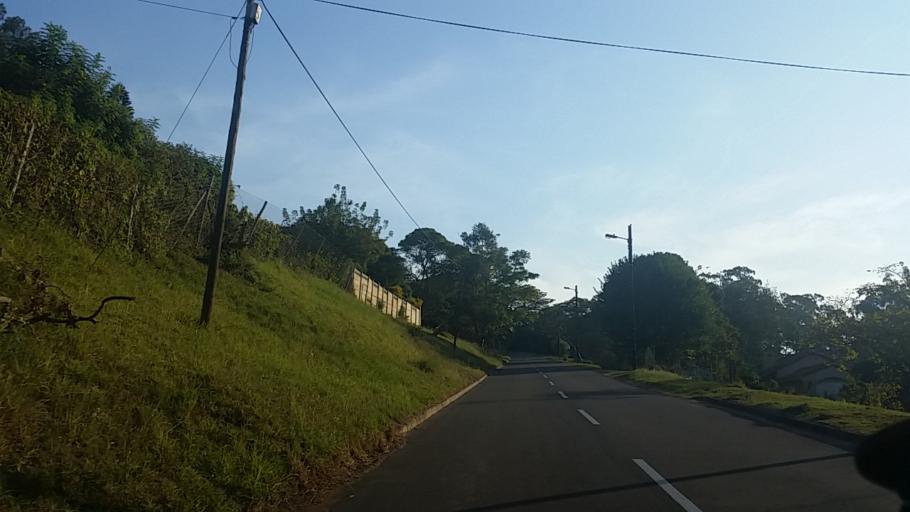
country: ZA
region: KwaZulu-Natal
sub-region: eThekwini Metropolitan Municipality
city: Berea
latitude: -29.8484
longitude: 30.9141
